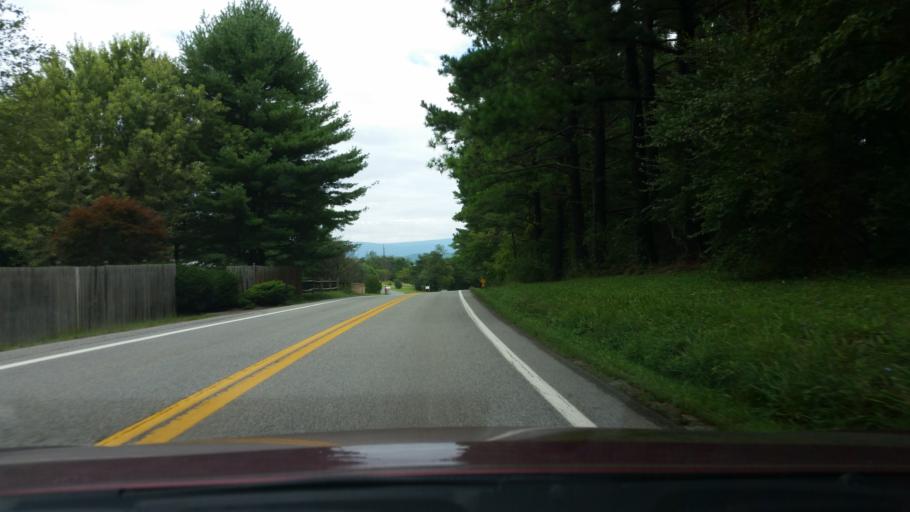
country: US
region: Maryland
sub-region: Washington County
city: Hancock
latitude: 39.6361
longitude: -78.1411
